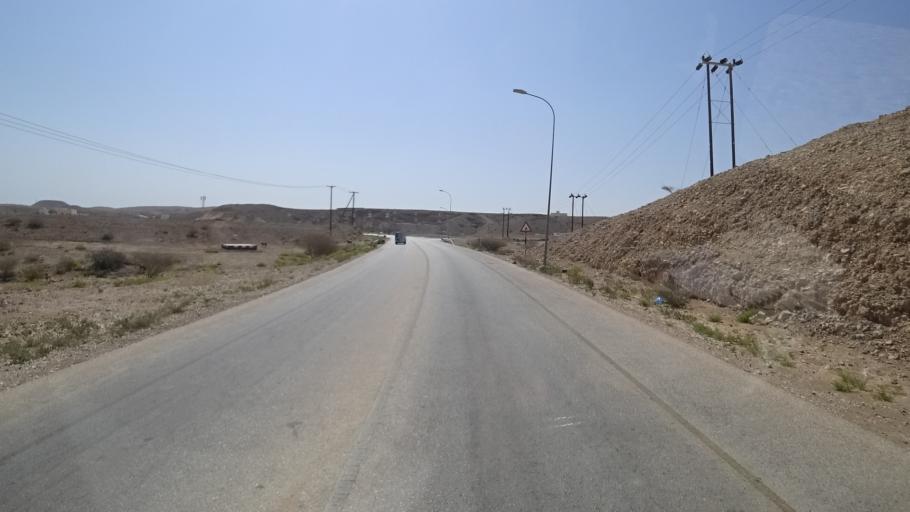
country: OM
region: Ash Sharqiyah
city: Sur
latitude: 22.5429
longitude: 59.5033
